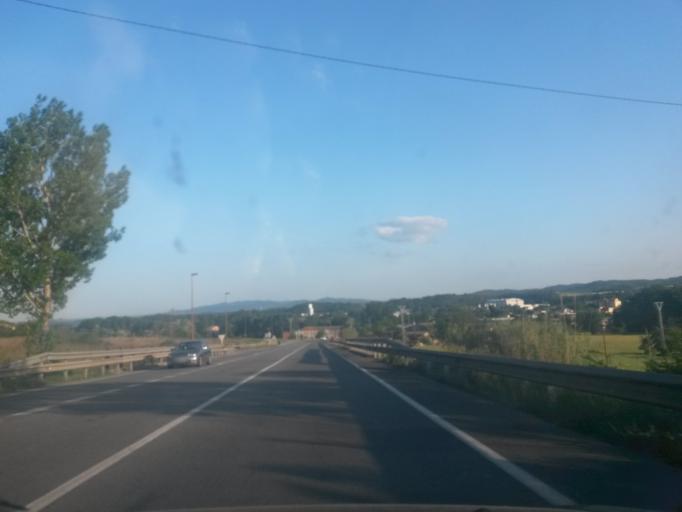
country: ES
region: Catalonia
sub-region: Provincia de Girona
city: Fontcoberta
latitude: 42.1047
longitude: 2.7955
